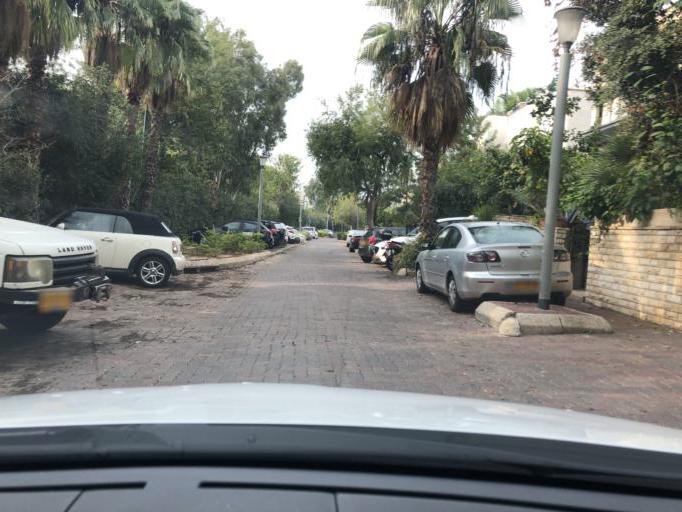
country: IL
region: Tel Aviv
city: Giv`atayim
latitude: 32.0547
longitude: 34.8252
